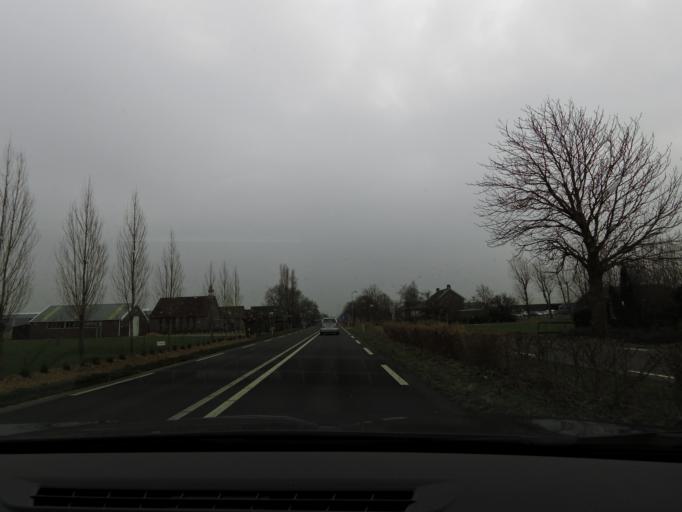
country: NL
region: South Holland
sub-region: Gemeente Nieuwkoop
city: Nieuwkoop
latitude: 52.1665
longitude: 4.7757
